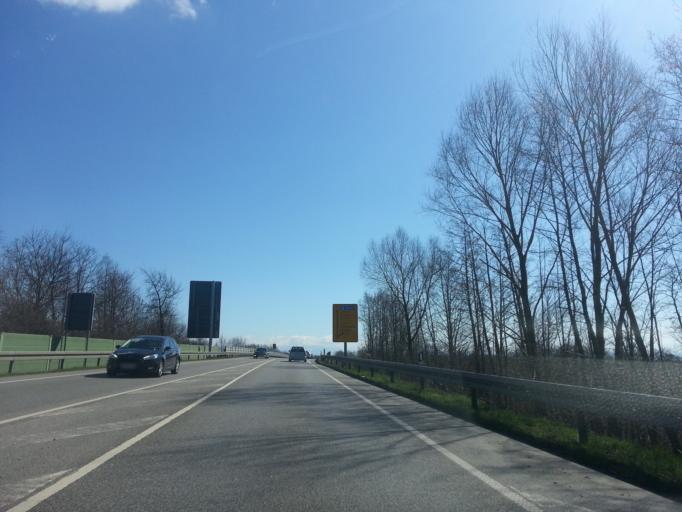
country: DE
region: Baden-Wuerttemberg
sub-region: Tuebingen Region
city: Friedrichshafen
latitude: 47.6622
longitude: 9.4960
